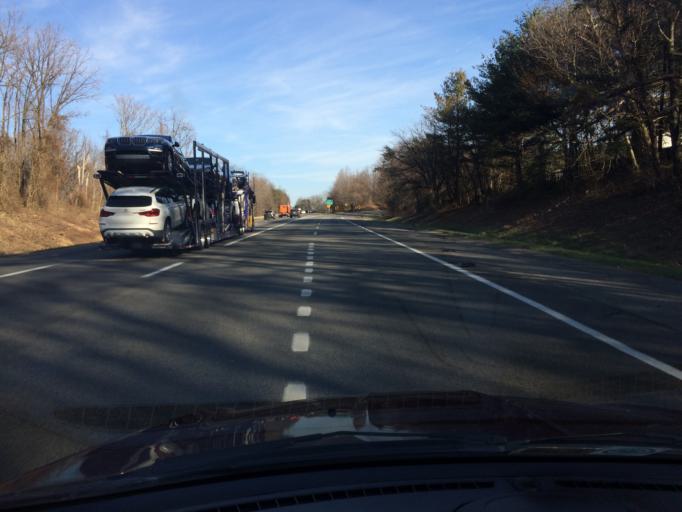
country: US
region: Virginia
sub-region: Roanoke County
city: Hollins
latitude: 37.3390
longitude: -80.0032
